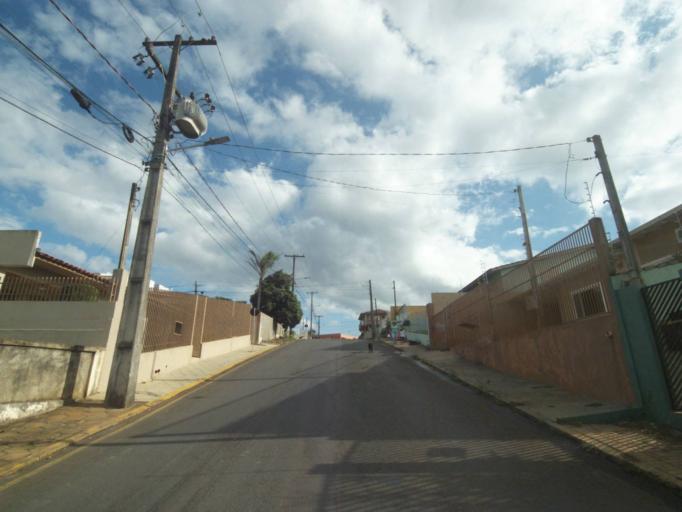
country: BR
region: Parana
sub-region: Telemaco Borba
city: Telemaco Borba
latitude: -24.3353
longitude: -50.6177
